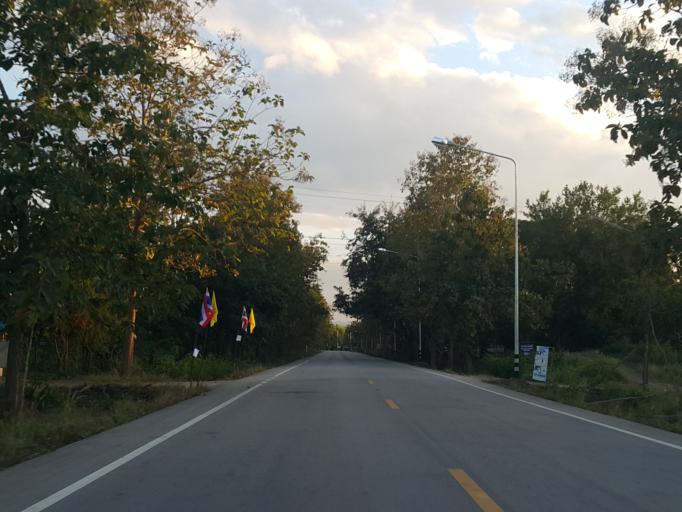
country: TH
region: Lampang
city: Mae Mo
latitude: 18.4530
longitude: 99.6345
